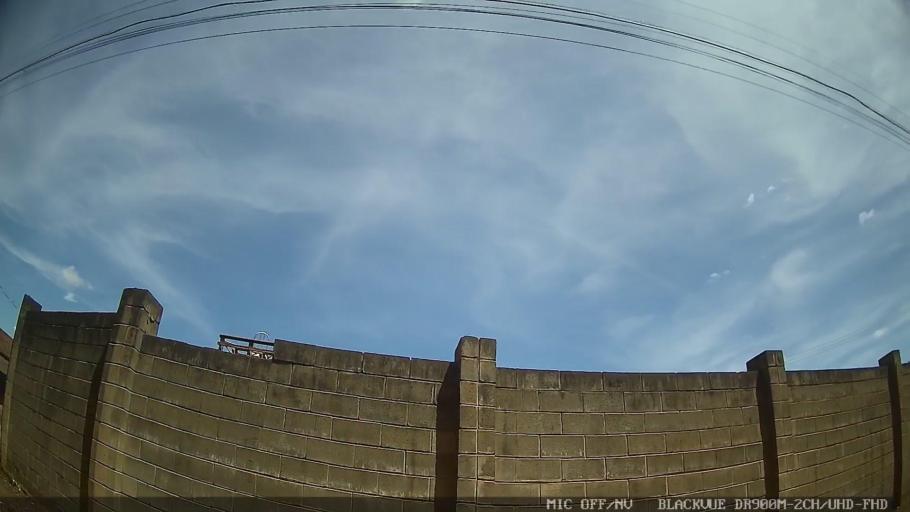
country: BR
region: Sao Paulo
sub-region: Jaguariuna
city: Jaguariuna
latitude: -22.6199
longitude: -47.0471
